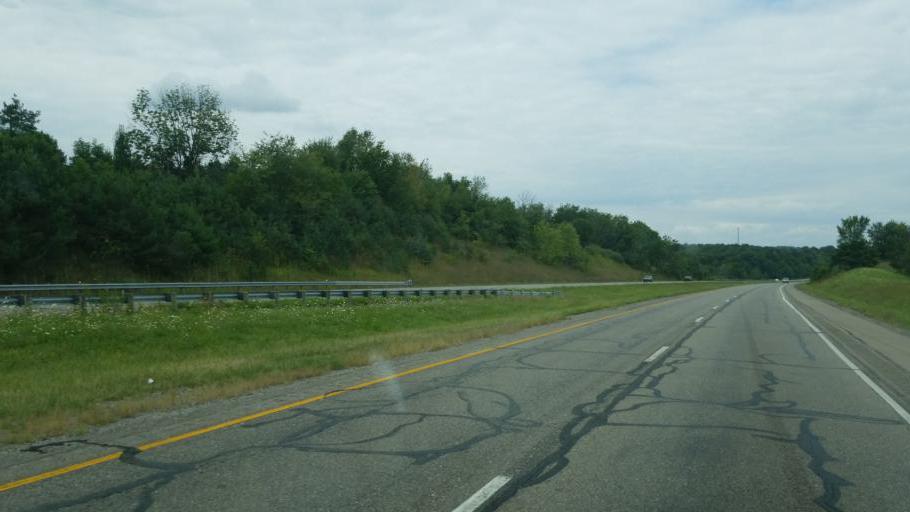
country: US
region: Ohio
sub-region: Columbiana County
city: Lisbon
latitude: 40.7975
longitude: -80.7450
